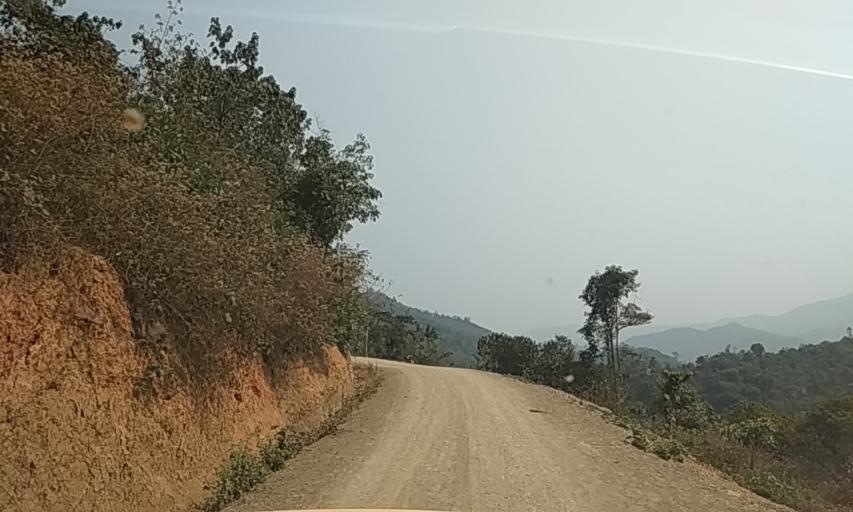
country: LA
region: Phongsali
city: Phongsali
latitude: 21.4778
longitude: 102.4423
